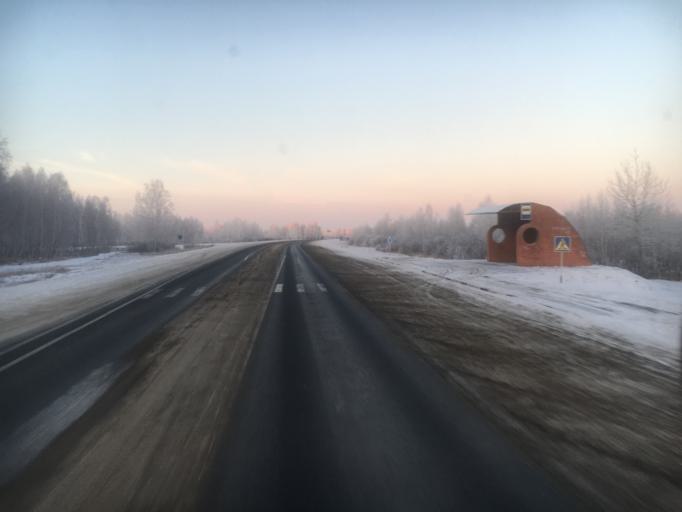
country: KZ
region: Soltustik Qazaqstan
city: Smirnovo
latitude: 54.4779
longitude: 69.2214
